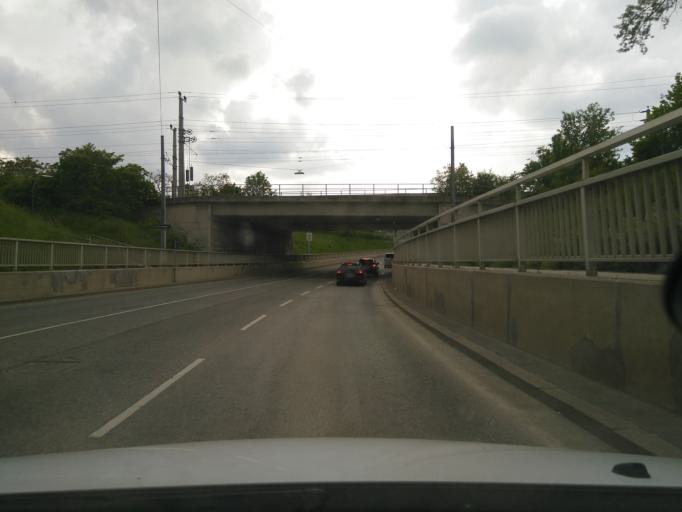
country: AT
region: Lower Austria
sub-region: Politischer Bezirk Modling
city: Perchtoldsdorf
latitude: 48.1519
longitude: 16.2935
